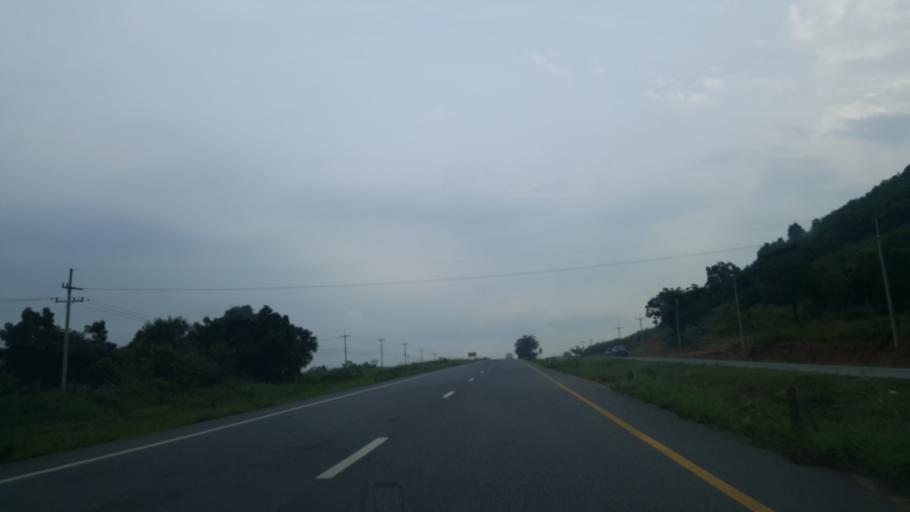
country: TH
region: Rayong
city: Ban Chang
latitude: 12.7572
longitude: 100.9917
